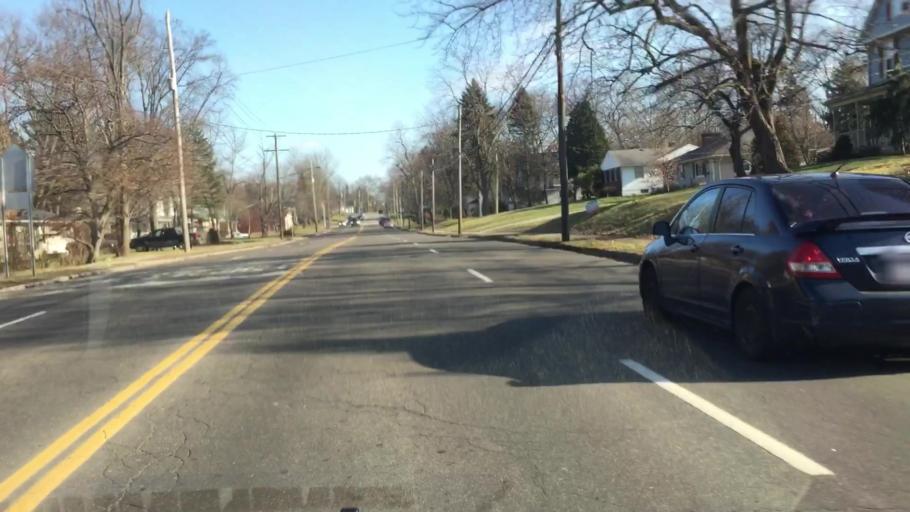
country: US
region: Ohio
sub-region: Summit County
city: Stow
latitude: 41.1594
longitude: -81.4331
